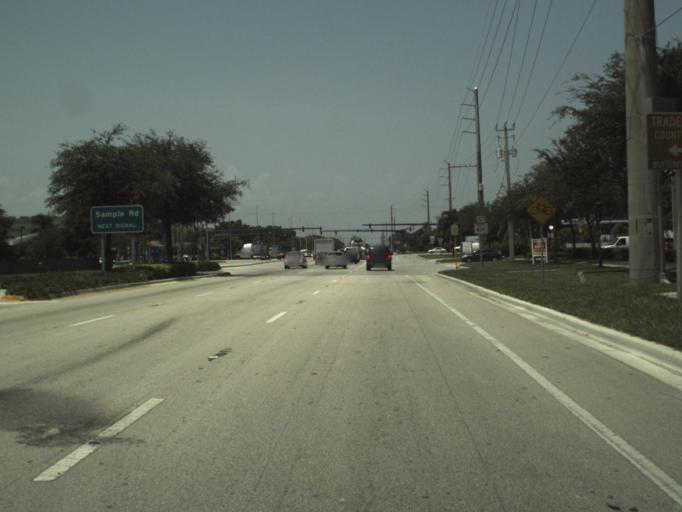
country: US
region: Florida
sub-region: Broward County
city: Tedder
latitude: 26.2725
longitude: -80.1520
